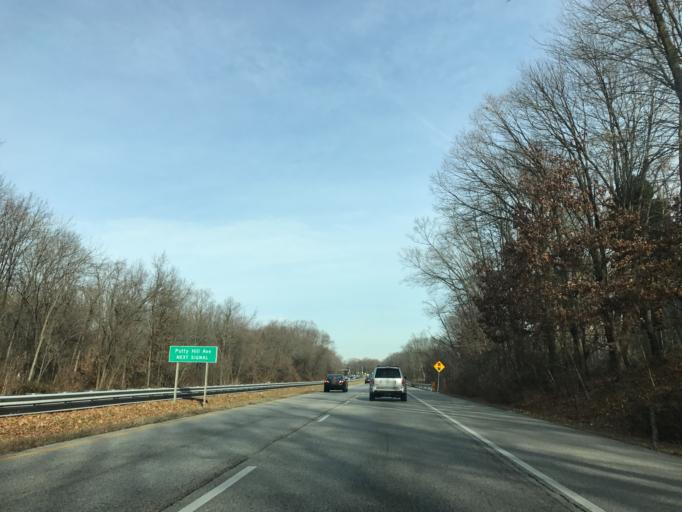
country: US
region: Maryland
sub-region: Baltimore County
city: Parkville
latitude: 39.3848
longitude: -76.5543
